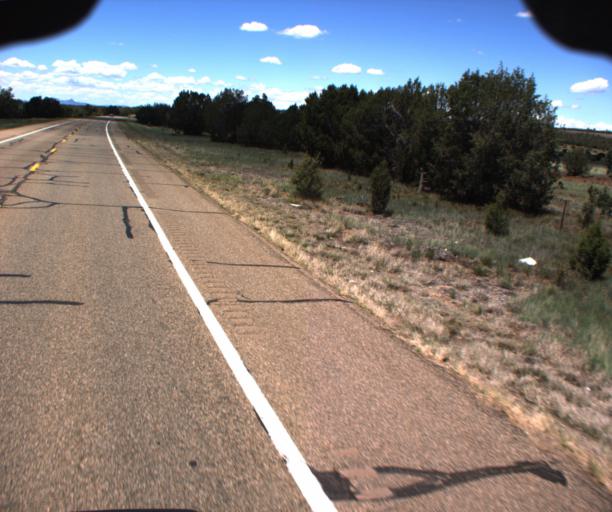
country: US
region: Arizona
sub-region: Yavapai County
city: Paulden
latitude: 35.0958
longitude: -112.4205
